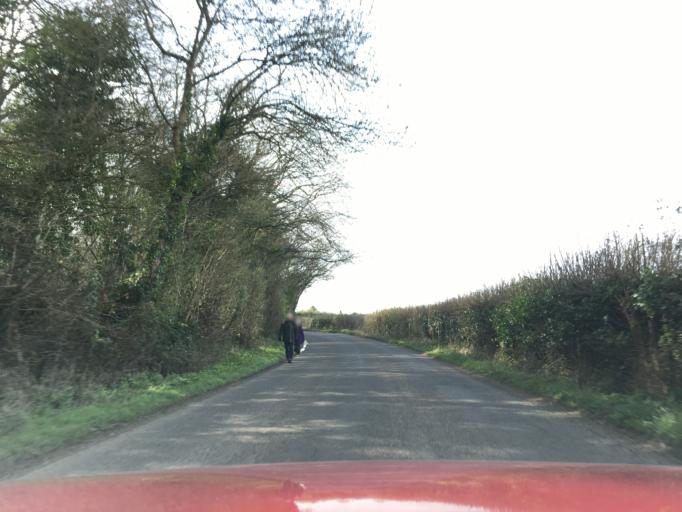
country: GB
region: England
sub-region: Wiltshire
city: Norton
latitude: 51.5207
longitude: -2.1499
